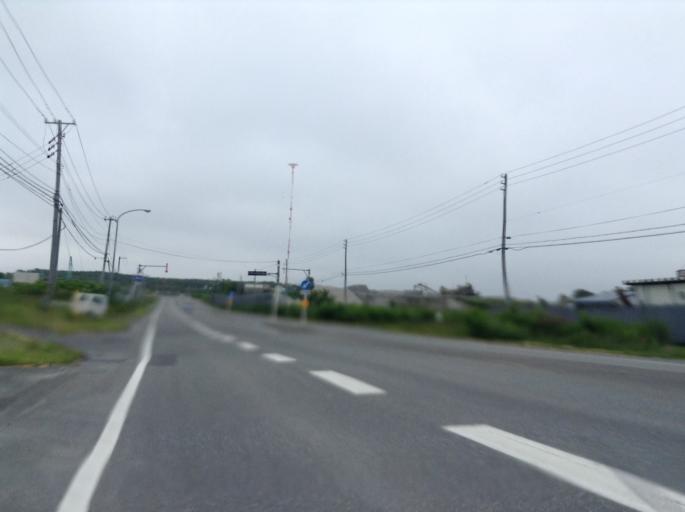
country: JP
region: Hokkaido
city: Wakkanai
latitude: 45.3793
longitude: 141.7103
